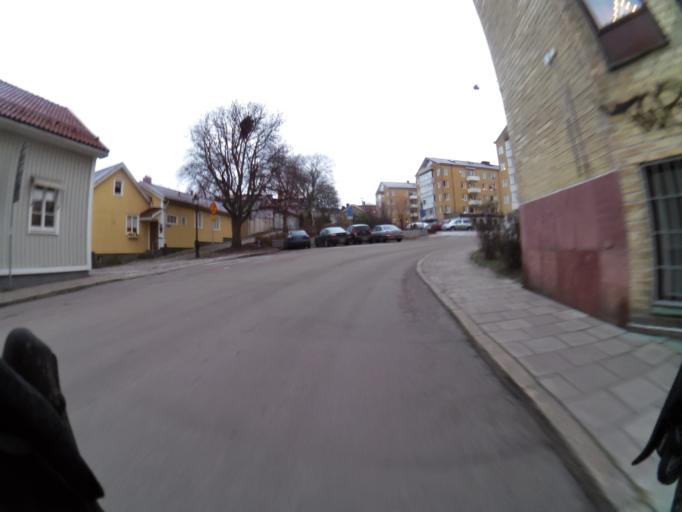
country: SE
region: Gaevleborg
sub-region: Gavle Kommun
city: Gavle
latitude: 60.6726
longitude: 17.1481
